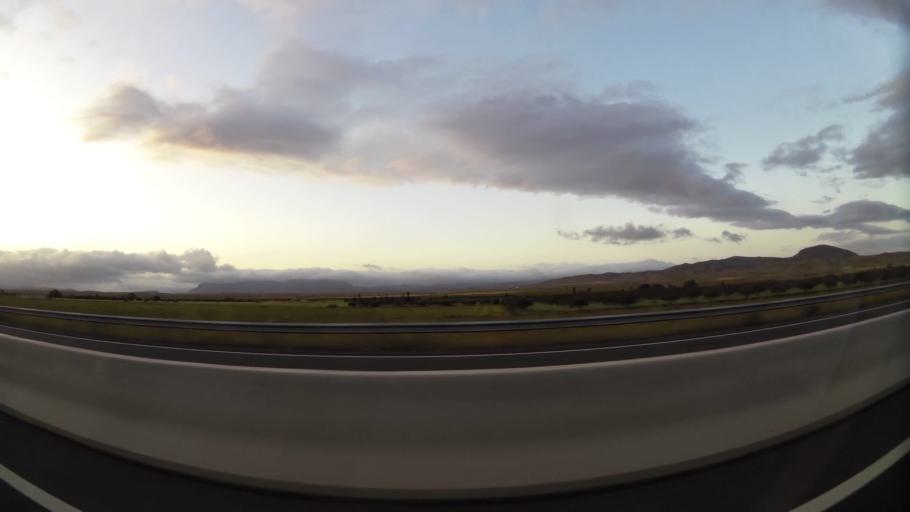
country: MA
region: Oriental
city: El Aioun
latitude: 34.5942
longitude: -2.7020
